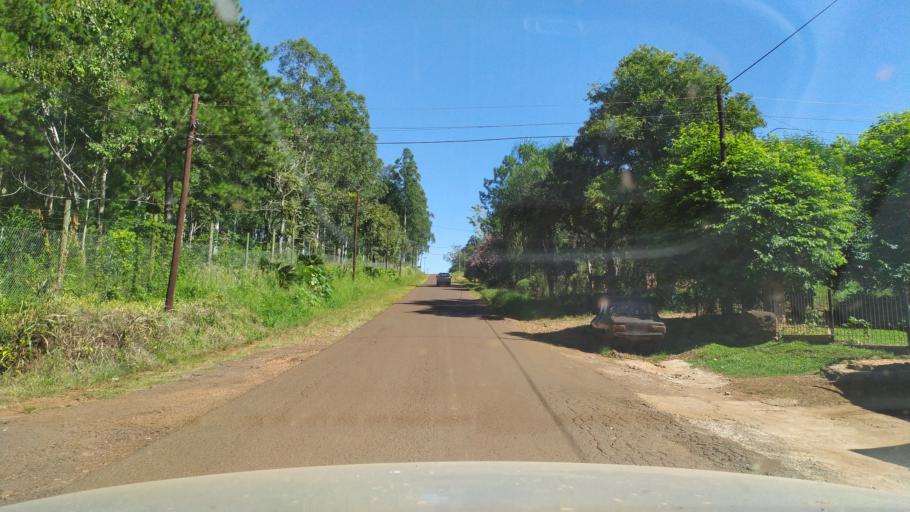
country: AR
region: Misiones
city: Caraguatay
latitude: -26.6493
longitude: -54.7462
